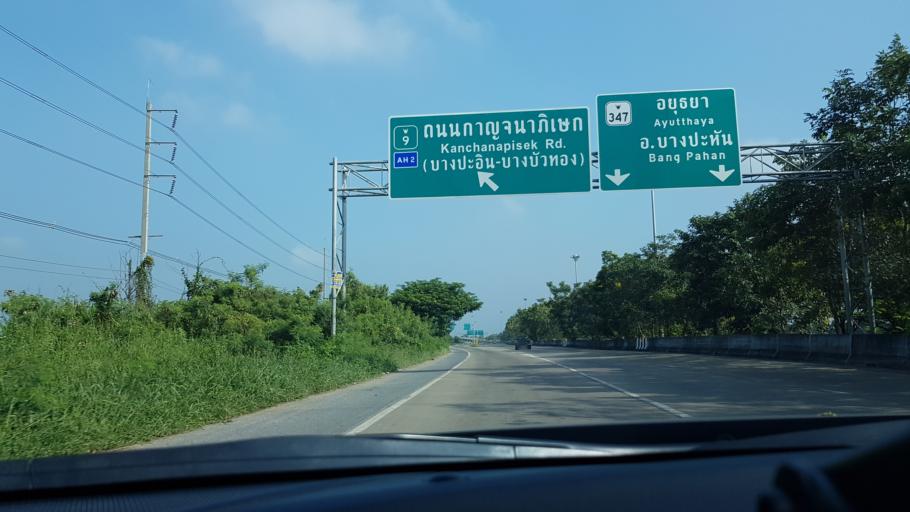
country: TH
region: Phra Nakhon Si Ayutthaya
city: Bang Pa-in
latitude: 14.1468
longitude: 100.5690
